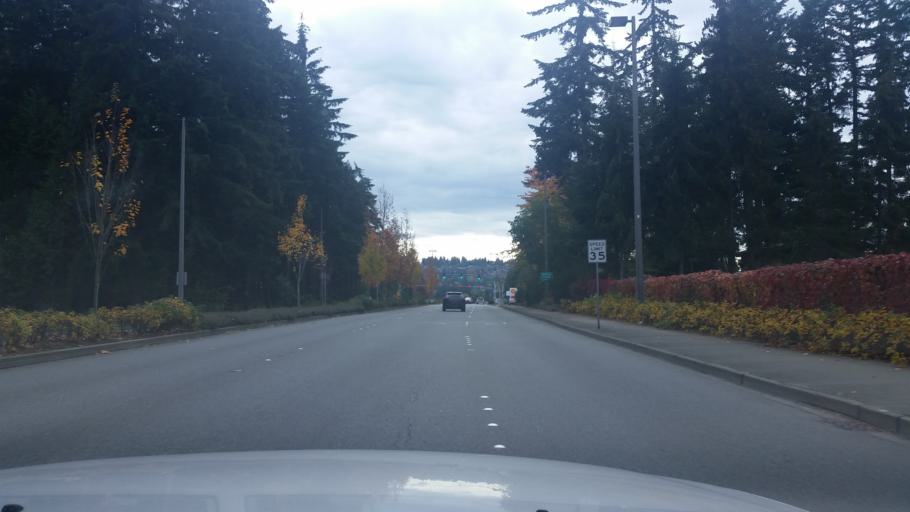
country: US
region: Washington
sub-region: King County
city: Eastgate
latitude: 47.5878
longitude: -122.1429
